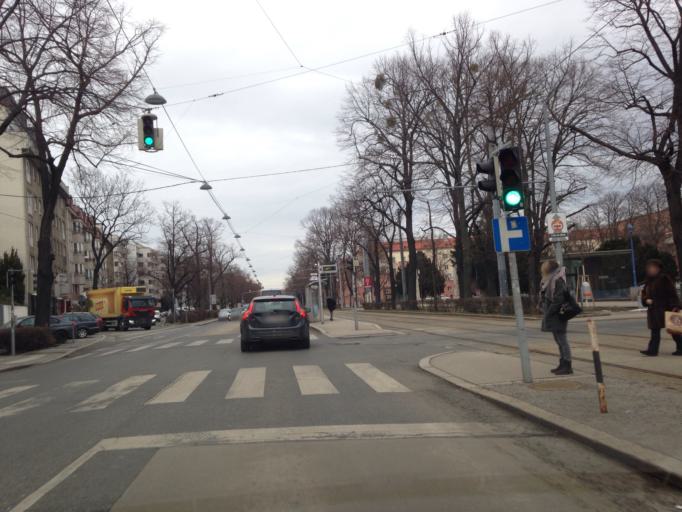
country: AT
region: Vienna
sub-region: Wien Stadt
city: Vienna
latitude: 48.2488
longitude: 16.3627
